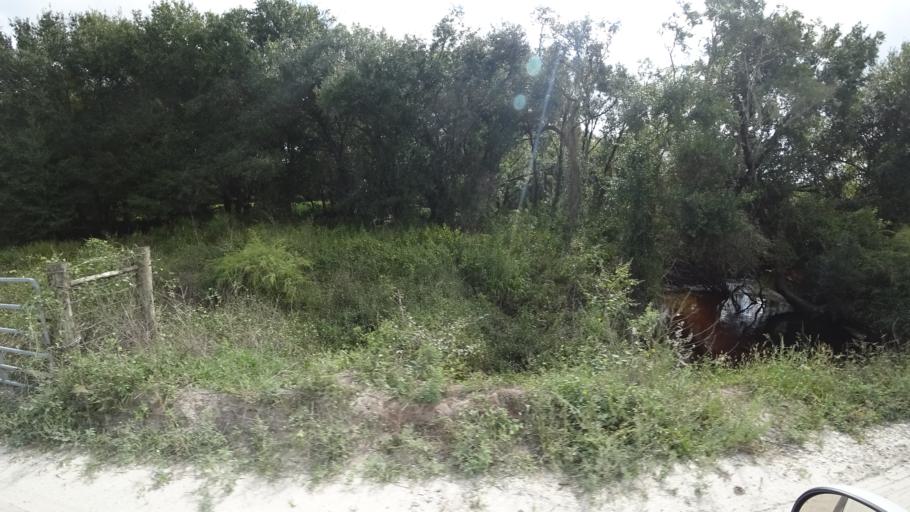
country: US
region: Florida
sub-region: Sarasota County
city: Lake Sarasota
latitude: 27.4241
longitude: -82.1867
